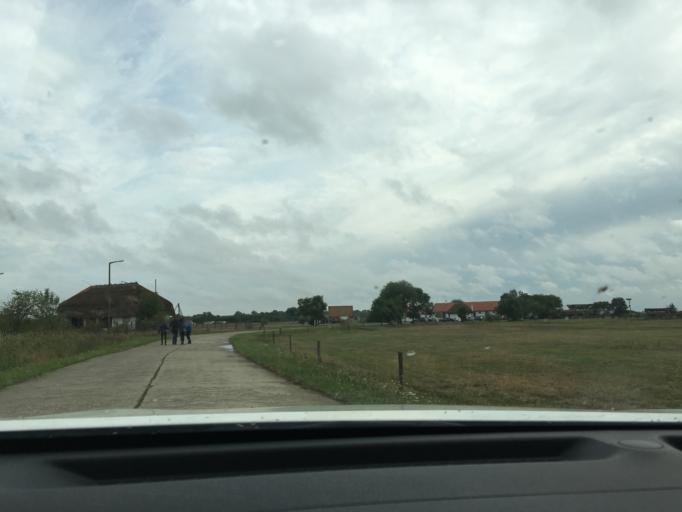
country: HU
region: Hajdu-Bihar
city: Hortobagy
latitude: 47.5751
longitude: 21.1454
